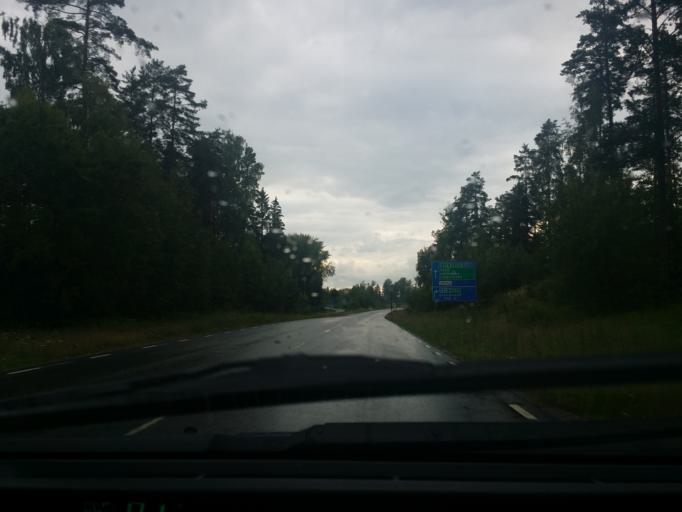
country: SE
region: Vaestmanland
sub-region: Arboga Kommun
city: Arboga
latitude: 59.4193
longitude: 15.8302
